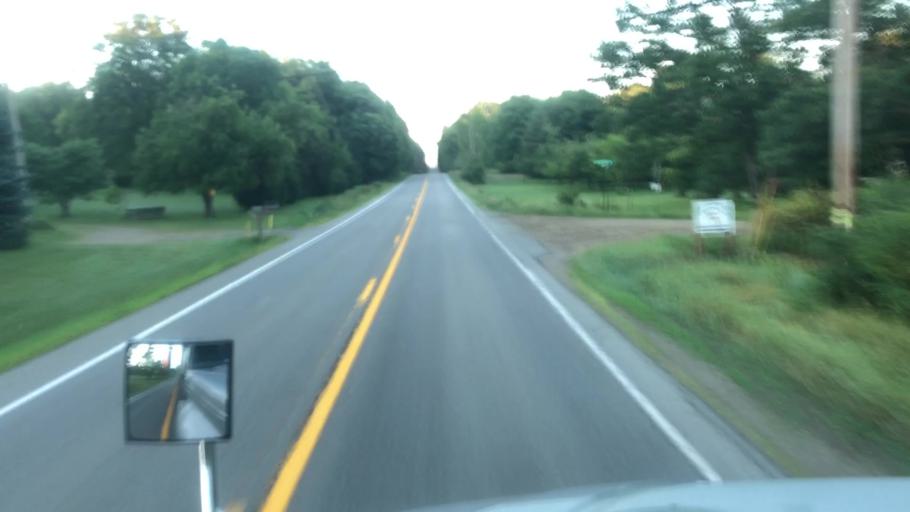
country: US
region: Pennsylvania
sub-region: Crawford County
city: Titusville
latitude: 41.5591
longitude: -79.6111
